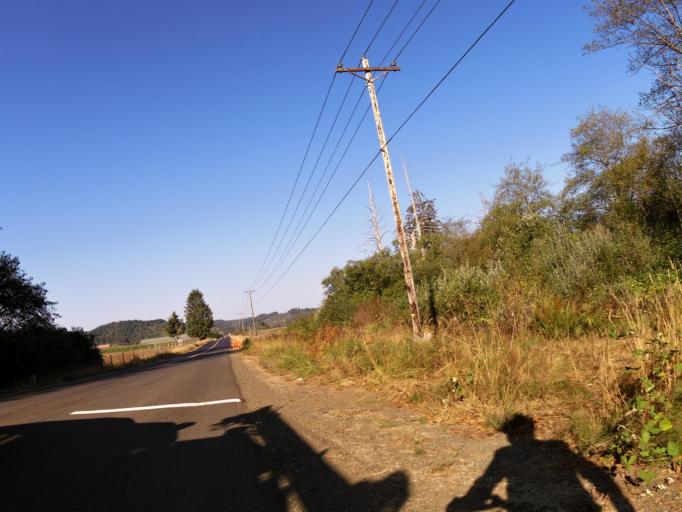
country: US
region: Oregon
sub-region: Tillamook County
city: Tillamook
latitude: 45.4015
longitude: -123.7943
